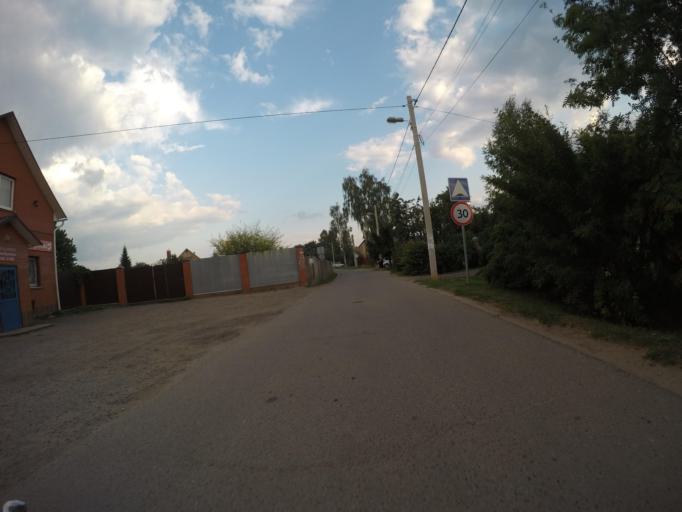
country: RU
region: Moskovskaya
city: Rechitsy
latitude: 55.5966
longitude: 38.5142
